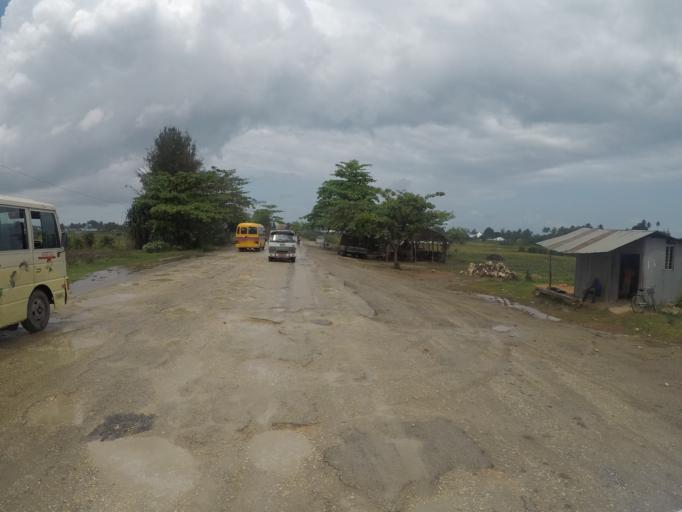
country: TZ
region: Zanzibar Central/South
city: Koani
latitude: -6.0752
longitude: 39.2233
